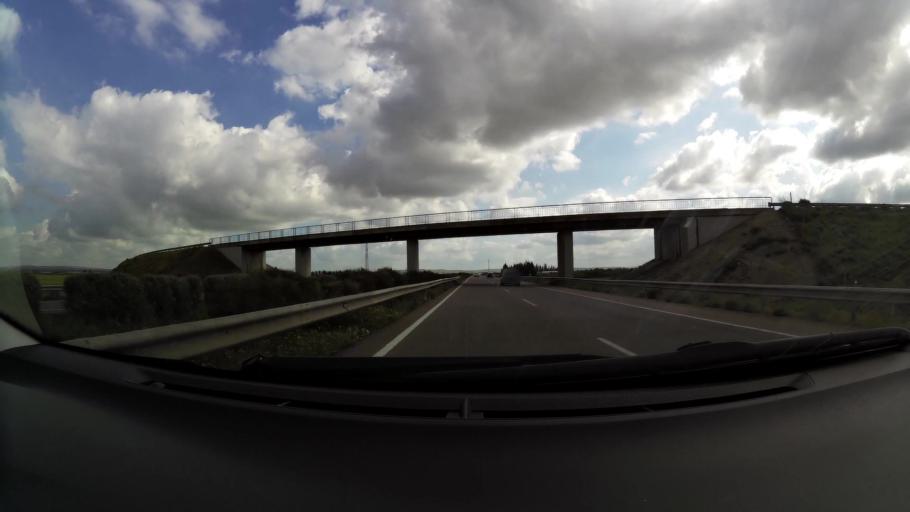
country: MA
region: Chaouia-Ouardigha
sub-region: Settat Province
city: Berrechid
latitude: 33.1469
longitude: -7.5736
